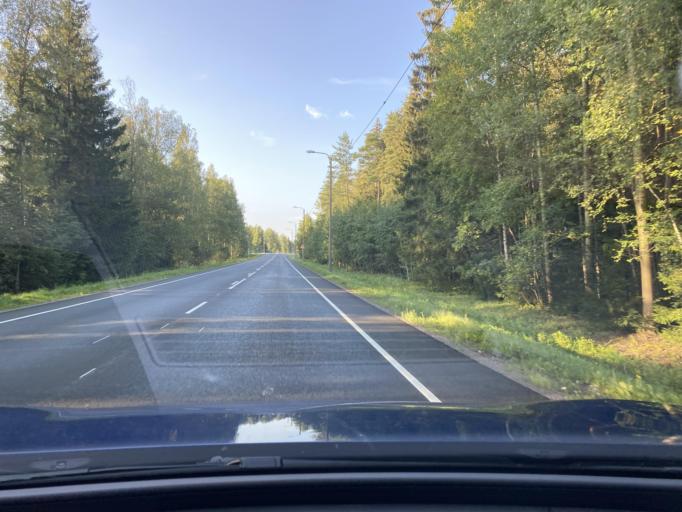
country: FI
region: Kymenlaakso
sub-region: Kouvola
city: Kouvola
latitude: 60.8915
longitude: 26.6044
